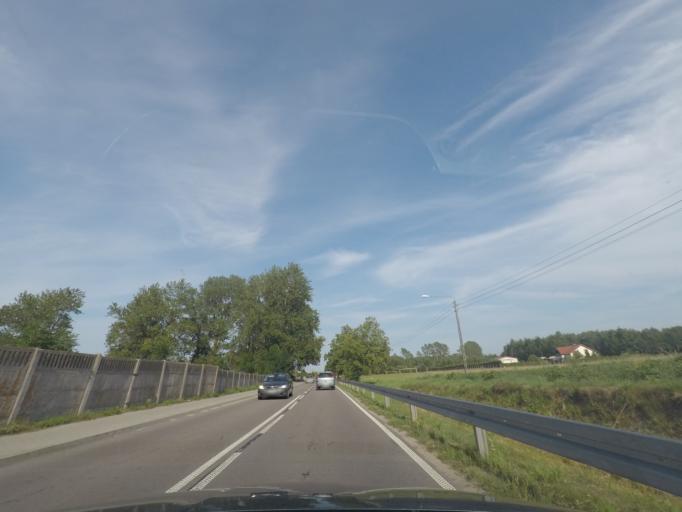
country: PL
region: Pomeranian Voivodeship
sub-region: Powiat leborski
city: Leba
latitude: 54.6448
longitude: 17.5465
